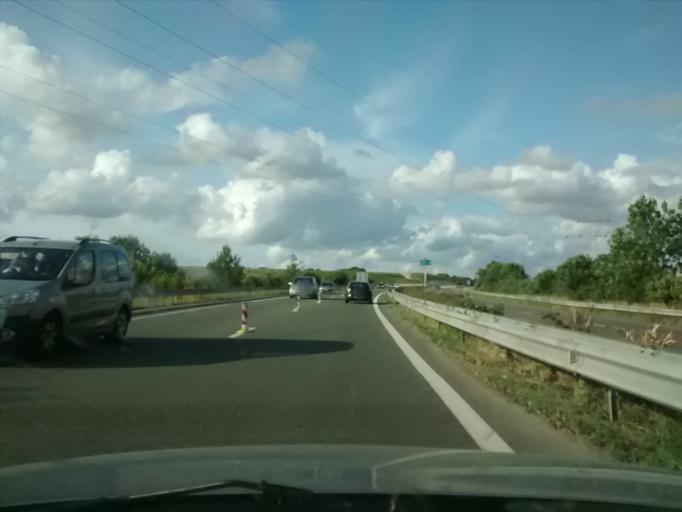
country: FR
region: Pays de la Loire
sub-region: Departement de la Mayenne
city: Saint-Jean-sur-Mayenne
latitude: 48.1056
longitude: -0.7459
